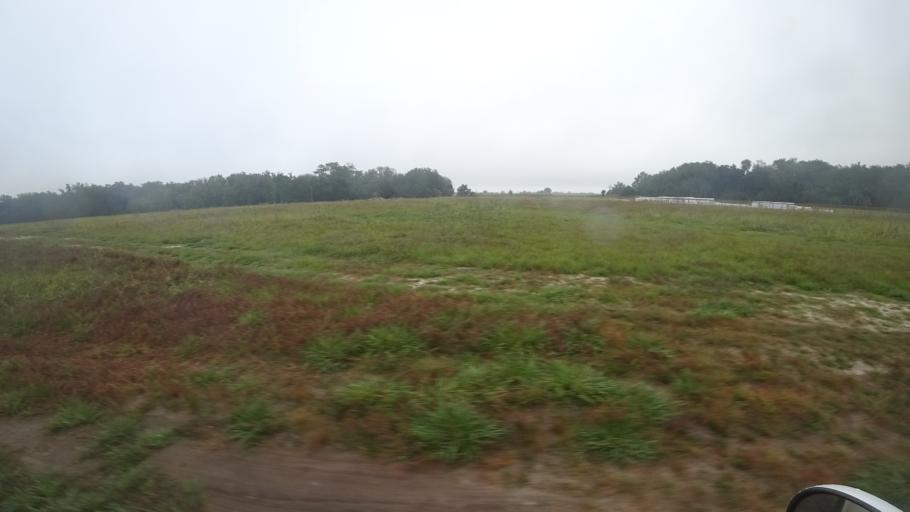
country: US
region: Florida
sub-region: Sarasota County
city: Lake Sarasota
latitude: 27.2912
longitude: -82.2160
